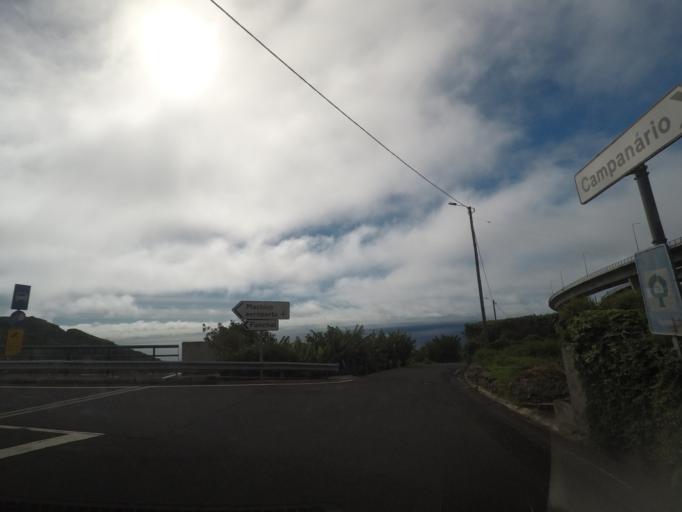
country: PT
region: Madeira
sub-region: Ribeira Brava
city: Campanario
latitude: 32.6655
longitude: -17.0326
